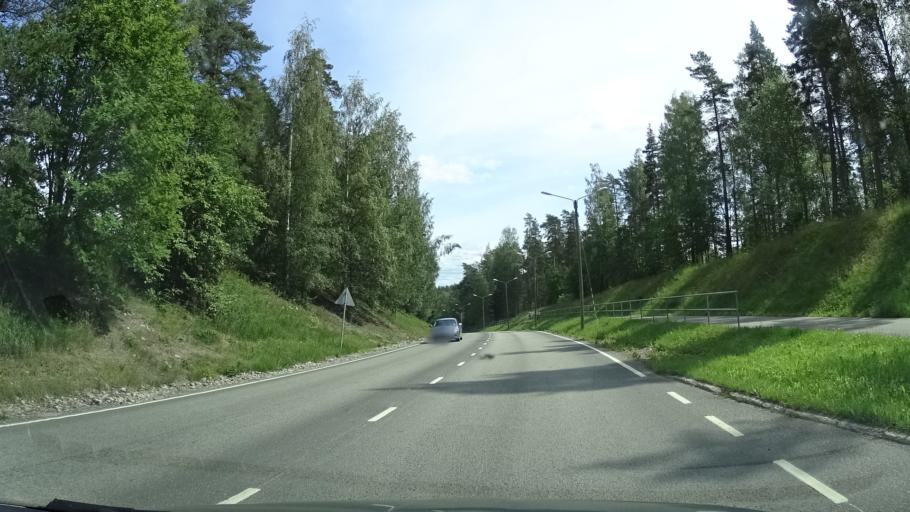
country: FI
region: Central Finland
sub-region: Jyvaeskylae
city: Jyvaeskylae
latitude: 62.2415
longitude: 25.6945
